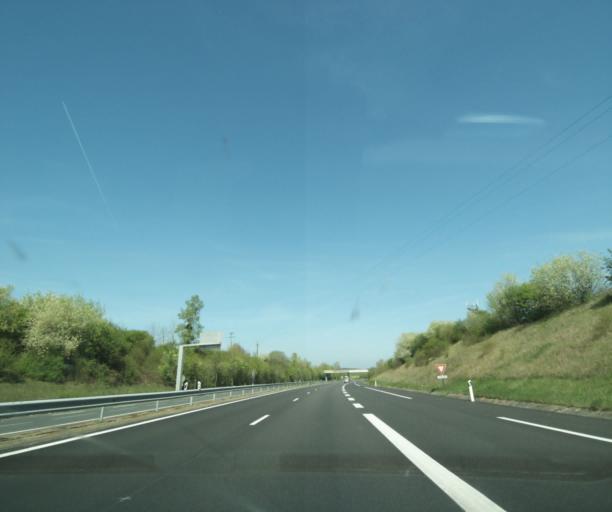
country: FR
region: Bourgogne
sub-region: Departement de la Nievre
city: La Charite-sur-Loire
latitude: 47.1373
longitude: 3.0433
